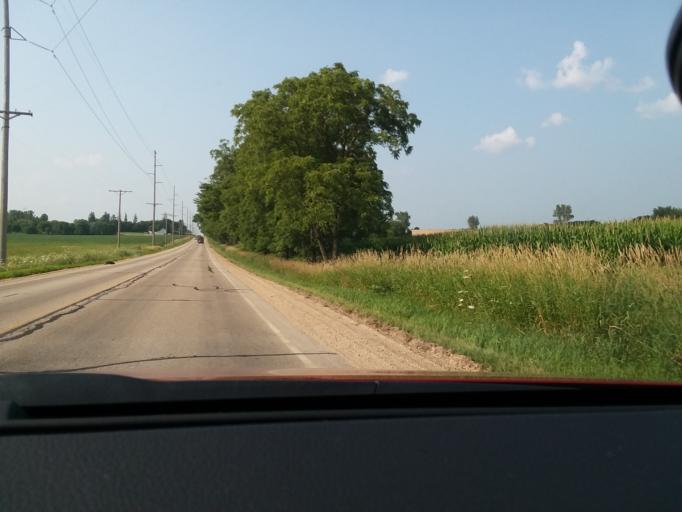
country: US
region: Wisconsin
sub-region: Dane County
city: Cottage Grove
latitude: 43.1214
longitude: -89.2664
